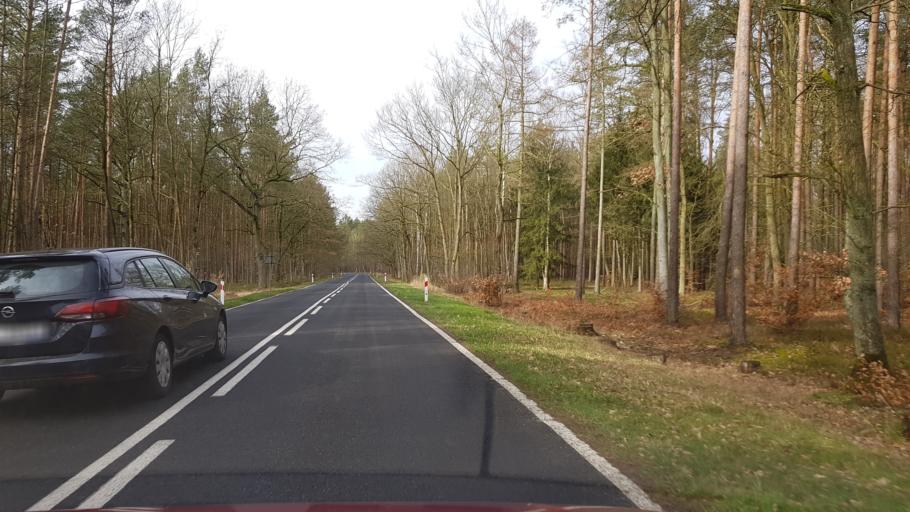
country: PL
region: West Pomeranian Voivodeship
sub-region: Powiat policki
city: Nowe Warpno
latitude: 53.6762
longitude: 14.3651
